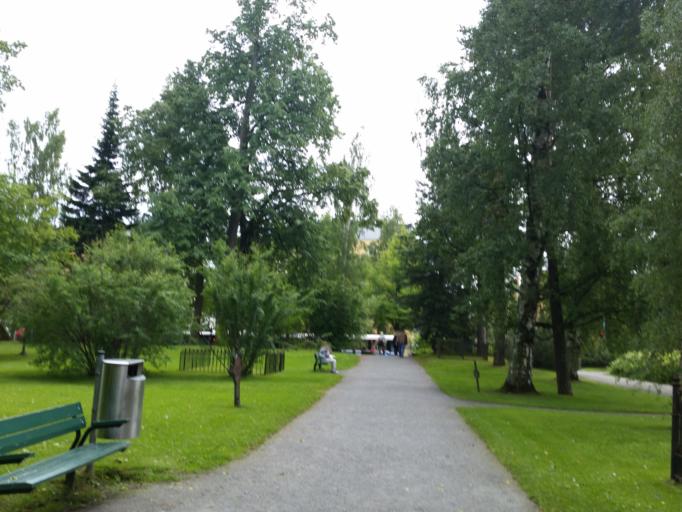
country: FI
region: Northern Savo
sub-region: Kuopio
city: Kuopio
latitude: 62.8936
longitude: 27.6742
